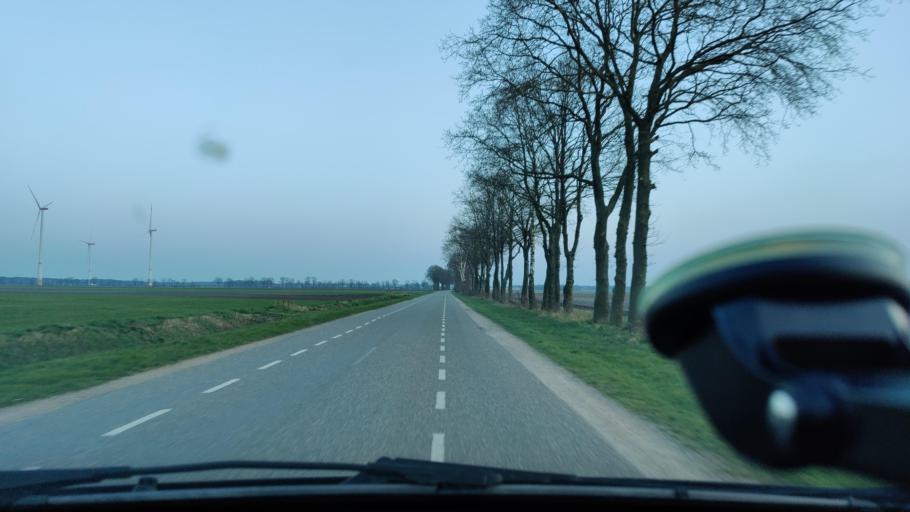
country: NL
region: Limburg
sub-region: Gemeente Bergen
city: Wellerlooi
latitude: 51.5655
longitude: 6.1462
